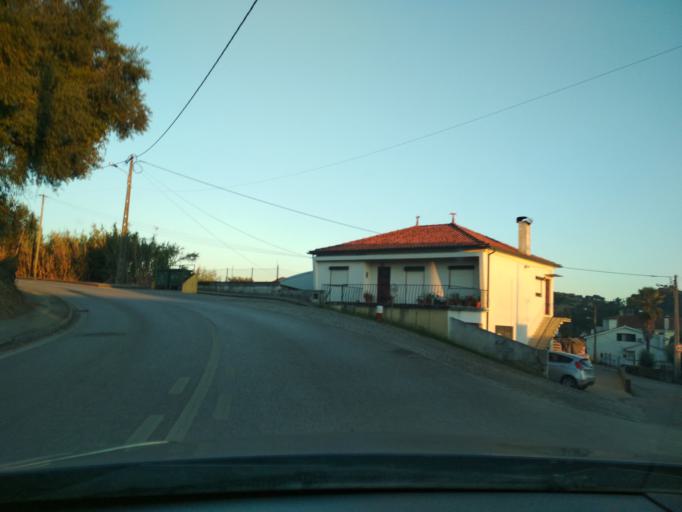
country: PT
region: Coimbra
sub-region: Coimbra
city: Coimbra
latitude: 40.1654
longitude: -8.4624
